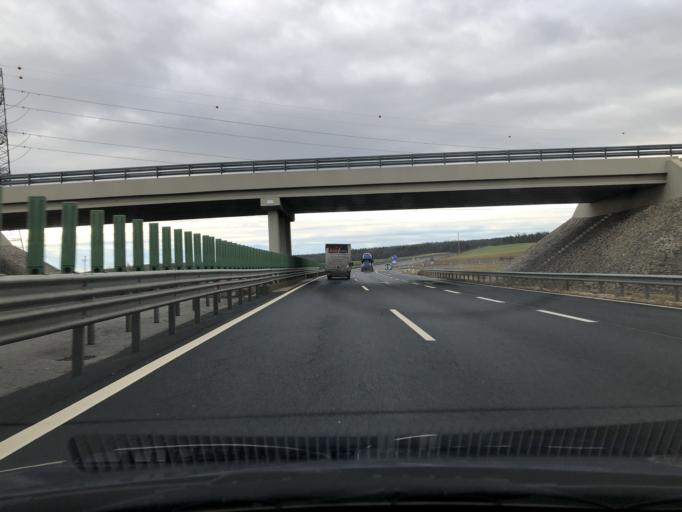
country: HU
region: Vas
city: Sarvar
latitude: 47.3031
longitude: 16.8378
